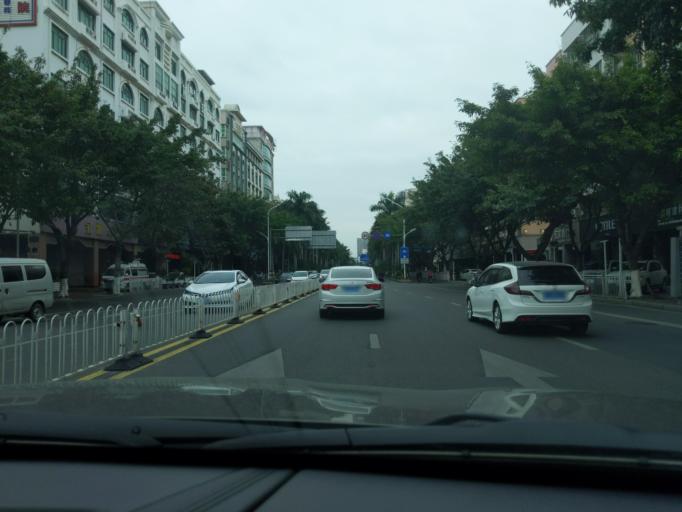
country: CN
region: Fujian
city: Shishi
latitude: 24.7415
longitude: 118.6380
